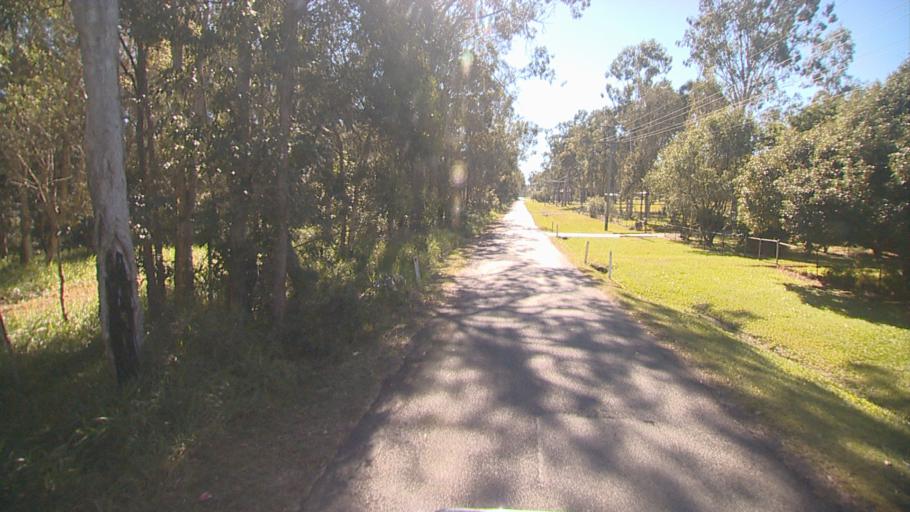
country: AU
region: Queensland
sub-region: Logan
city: Park Ridge South
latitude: -27.6962
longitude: 153.0044
